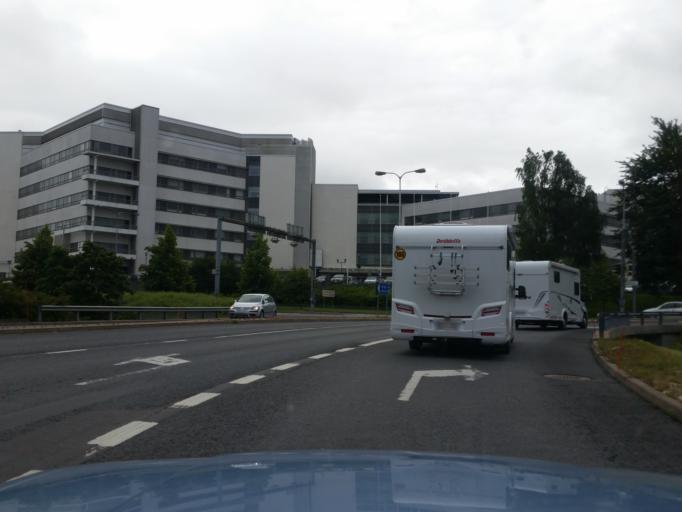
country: FI
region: Varsinais-Suomi
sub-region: Turku
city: Turku
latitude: 60.4554
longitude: 22.2943
